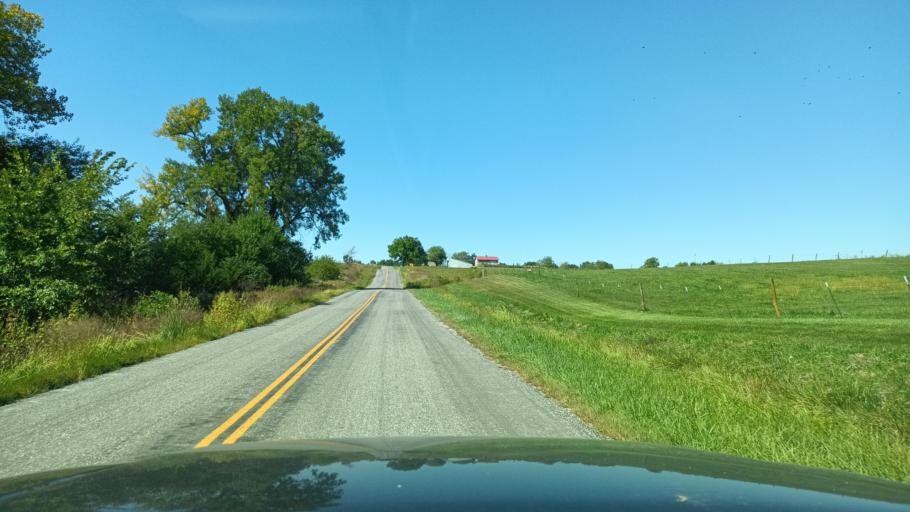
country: US
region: Missouri
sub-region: Adair County
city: Kirksville
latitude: 40.3298
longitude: -92.5574
